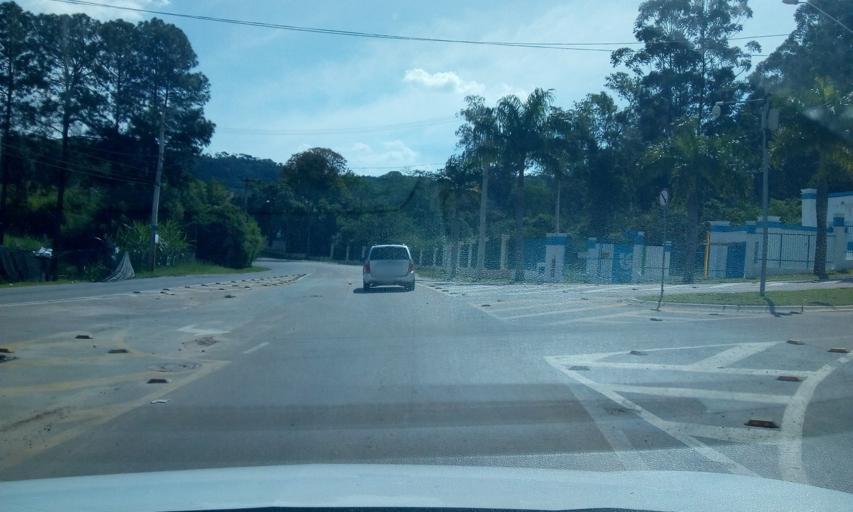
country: BR
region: Sao Paulo
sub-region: Itupeva
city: Itupeva
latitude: -23.1369
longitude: -47.0458
